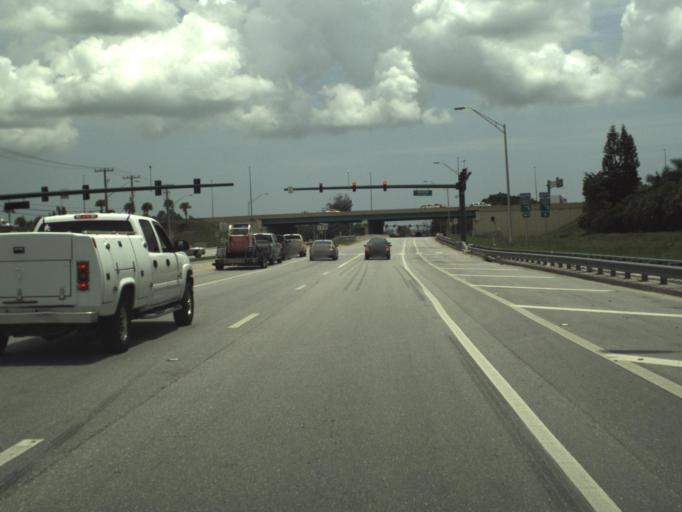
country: US
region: Florida
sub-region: Palm Beach County
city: Villages of Oriole
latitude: 26.4537
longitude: -80.1774
